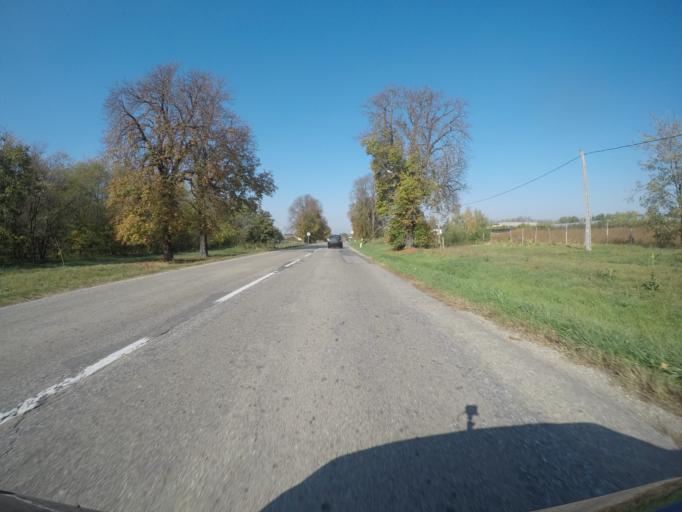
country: HU
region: Tolna
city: Szedres
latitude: 46.4682
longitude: 18.6869
